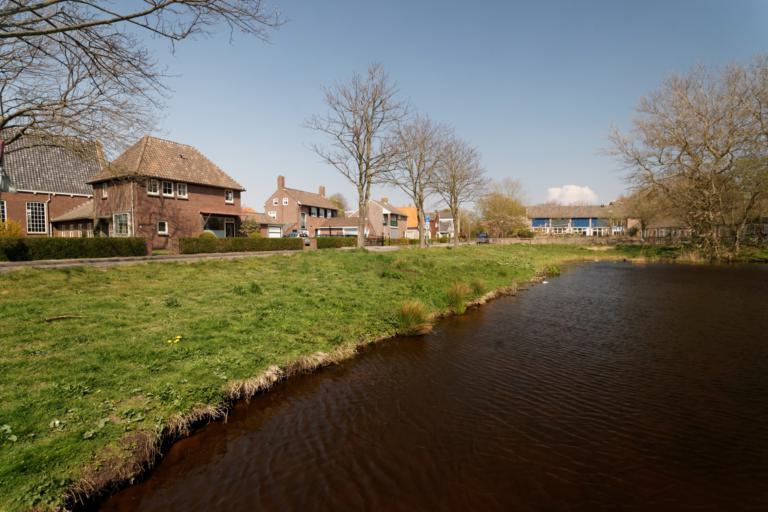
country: NL
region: North Holland
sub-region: Gemeente Texel
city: Den Burg
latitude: 53.0524
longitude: 4.7977
